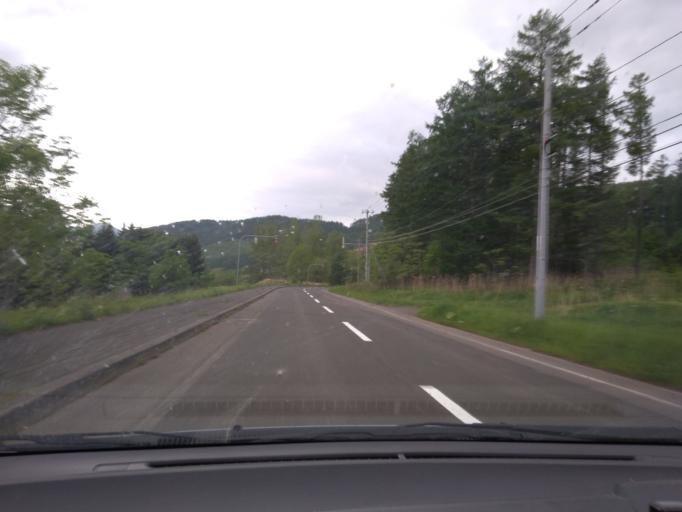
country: JP
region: Hokkaido
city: Shimo-furano
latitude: 43.1744
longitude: 142.5190
